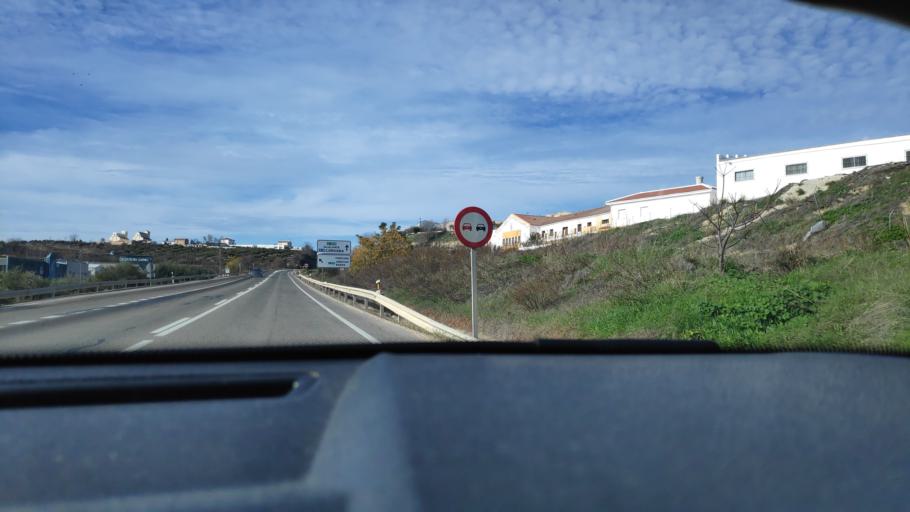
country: ES
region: Andalusia
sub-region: Provincia de Jaen
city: Porcuna
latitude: 37.8691
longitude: -4.1662
